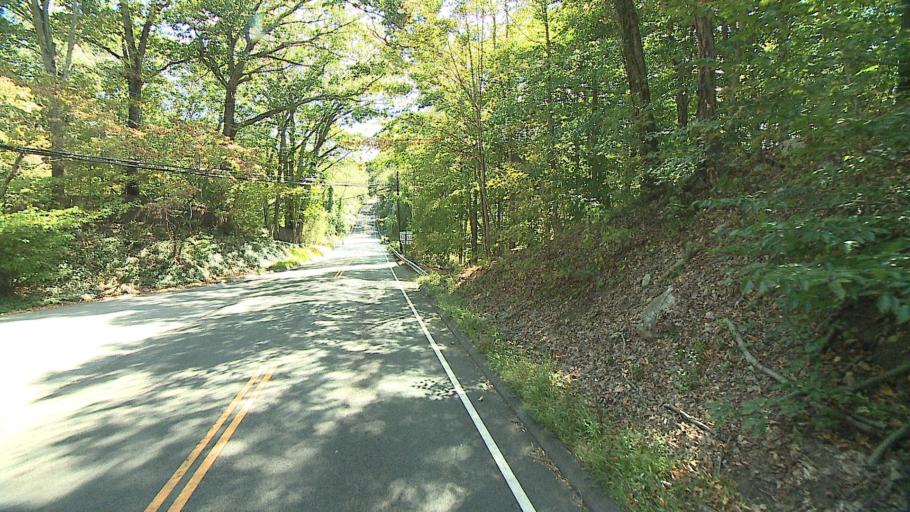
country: US
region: Connecticut
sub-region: Fairfield County
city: Wilton
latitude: 41.1952
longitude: -73.4015
